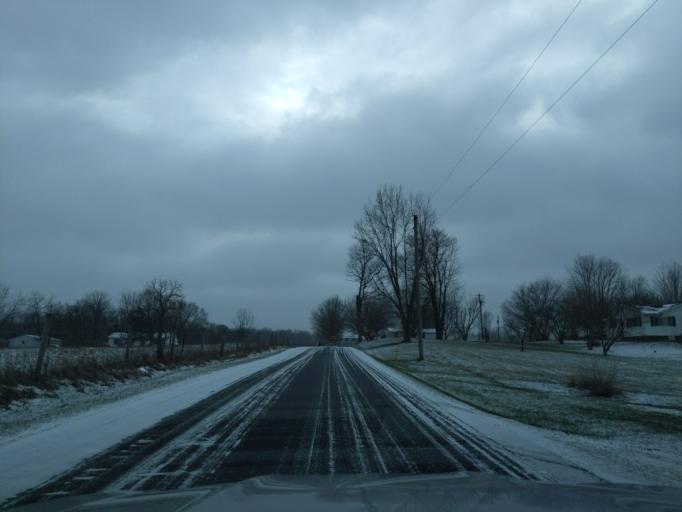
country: US
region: Indiana
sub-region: Decatur County
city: Westport
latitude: 39.2204
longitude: -85.5175
